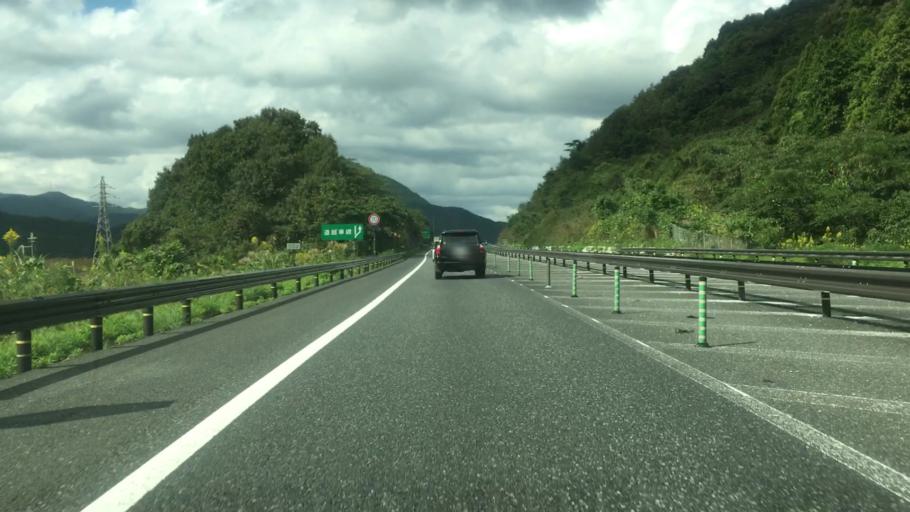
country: JP
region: Kyoto
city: Fukuchiyama
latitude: 35.2359
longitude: 135.0182
